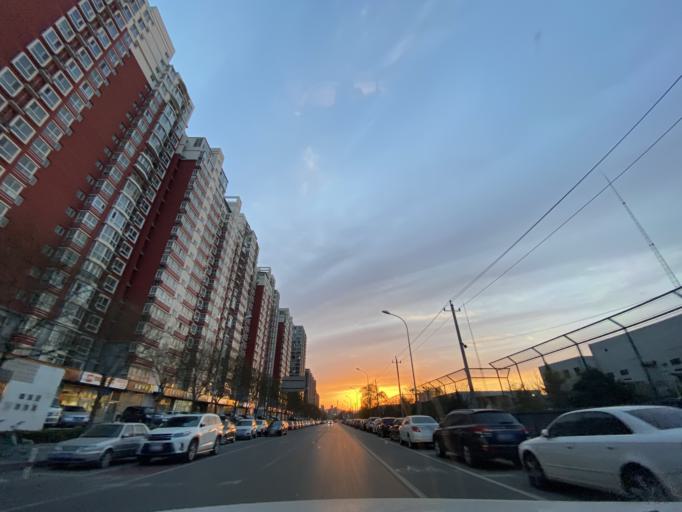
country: CN
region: Beijing
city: Qinghe
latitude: 40.0163
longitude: 116.3661
